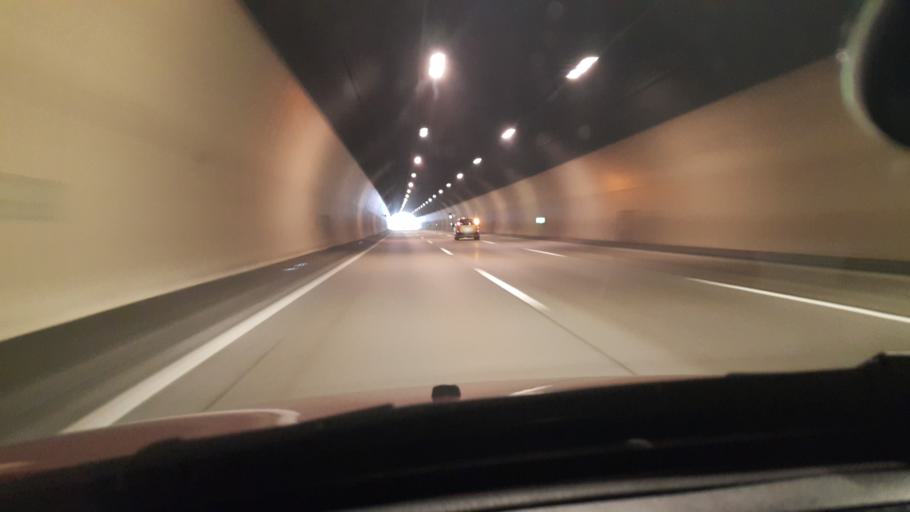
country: AT
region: Styria
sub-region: Politischer Bezirk Graz-Umgebung
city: Gratkorn
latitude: 47.1258
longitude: 15.3653
